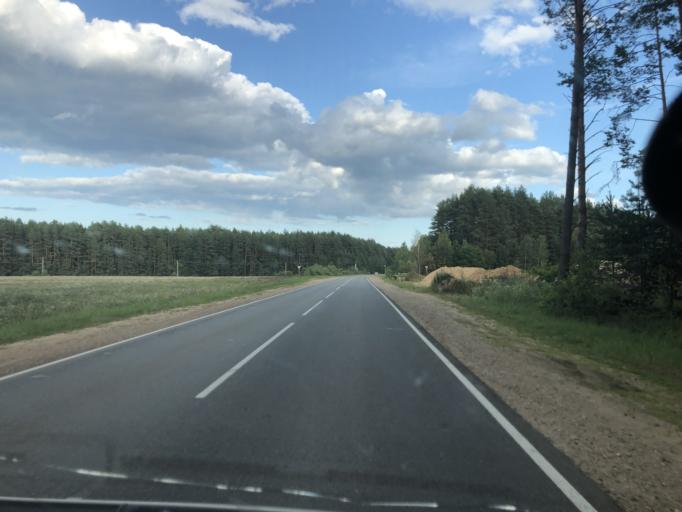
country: RU
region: Kaluga
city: Yukhnov
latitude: 54.7240
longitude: 35.2115
